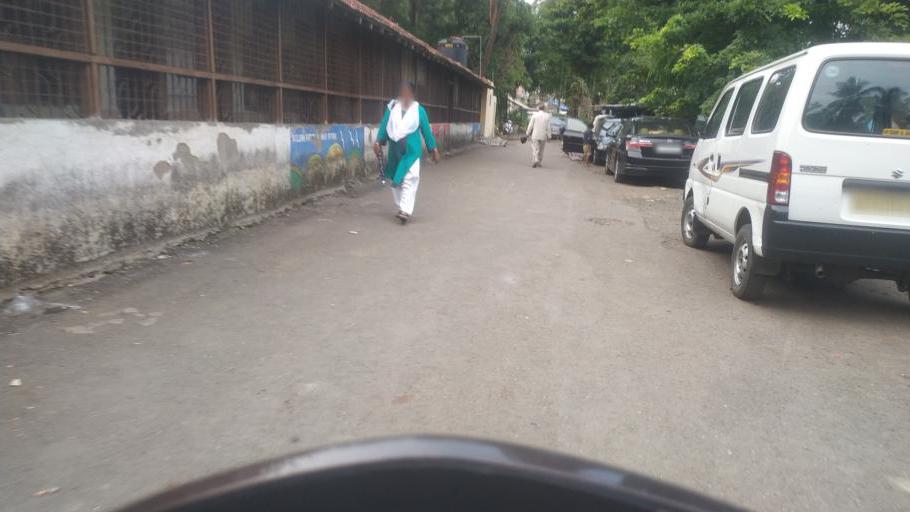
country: IN
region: Maharashtra
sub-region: Mumbai Suburban
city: Mumbai
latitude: 19.0116
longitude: 72.8550
